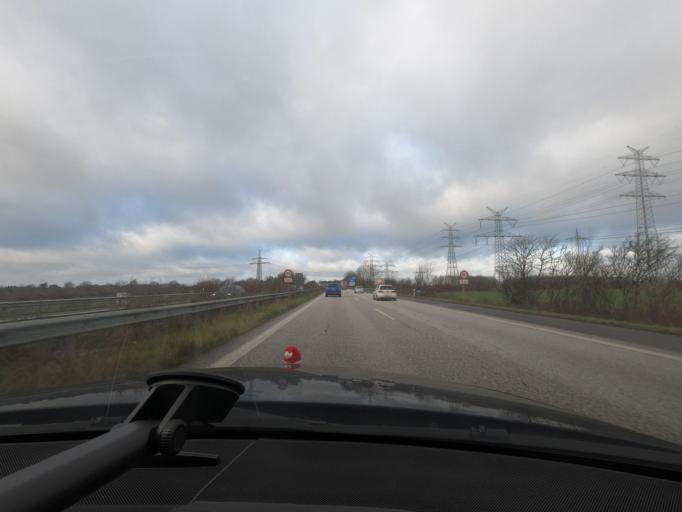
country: DE
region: Schleswig-Holstein
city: Schulldorf
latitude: 54.3166
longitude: 9.7448
